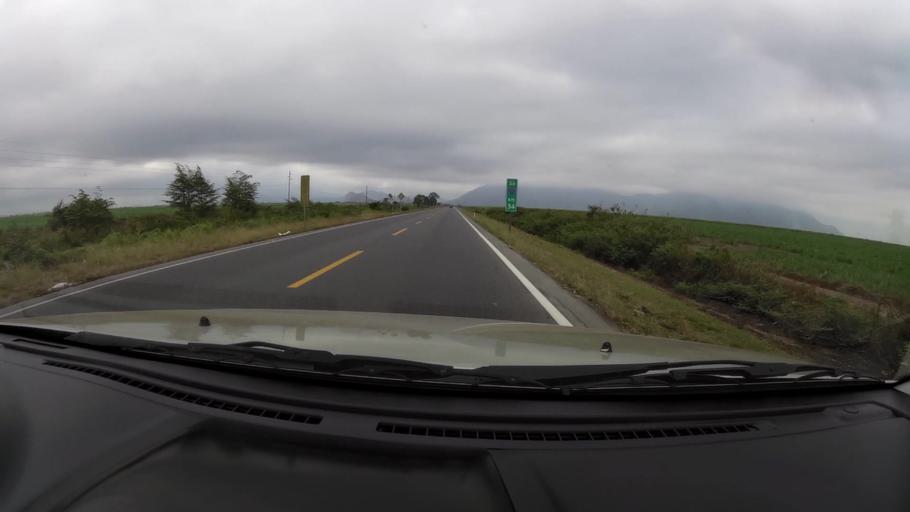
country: EC
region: Guayas
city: Naranjito
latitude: -2.3217
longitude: -79.6367
